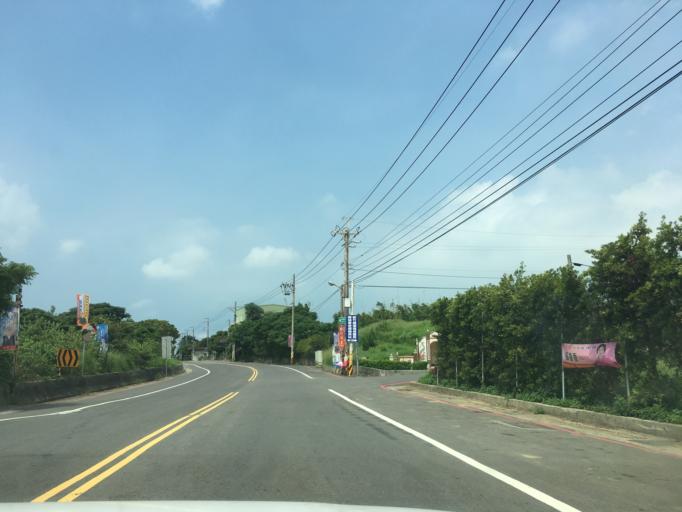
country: TW
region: Taiwan
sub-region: Hsinchu
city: Zhubei
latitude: 24.9045
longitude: 121.0237
